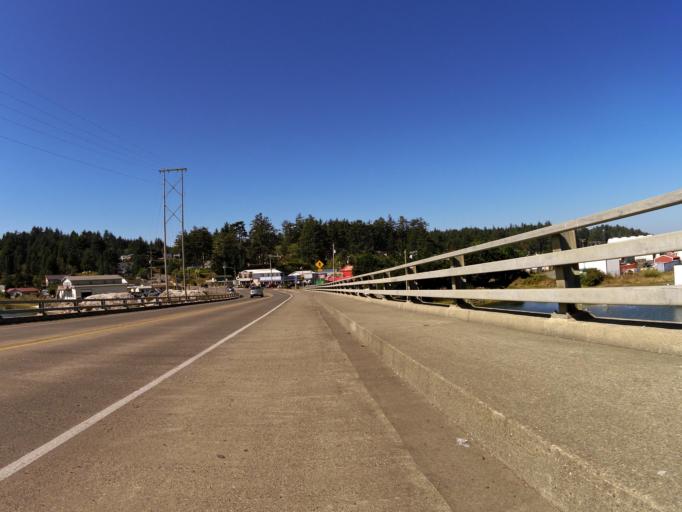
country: US
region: Oregon
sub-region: Coos County
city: Barview
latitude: 43.3392
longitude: -124.3224
